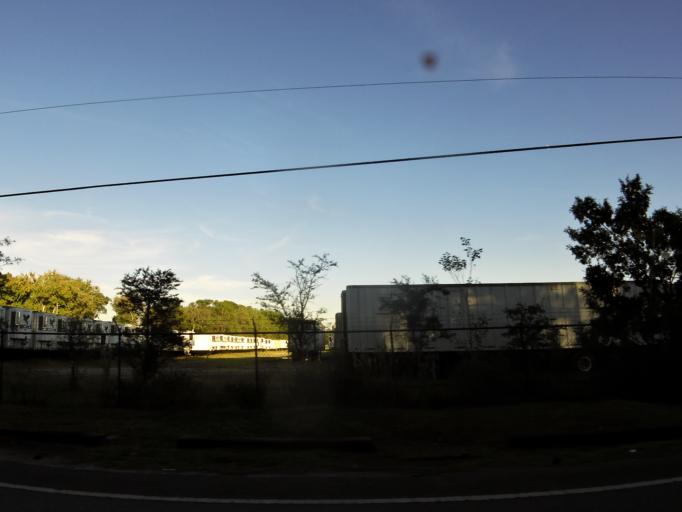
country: US
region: Florida
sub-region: Duval County
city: Jacksonville
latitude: 30.3584
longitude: -81.7647
